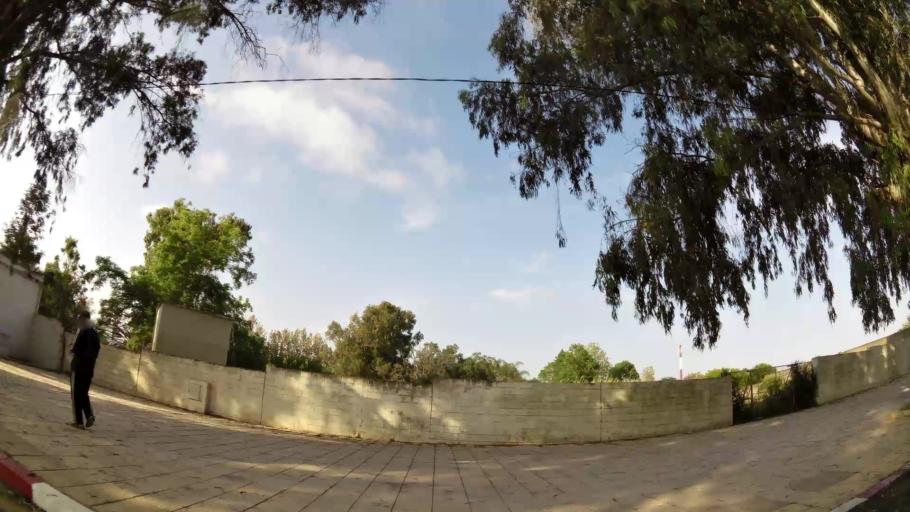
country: MA
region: Rabat-Sale-Zemmour-Zaer
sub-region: Rabat
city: Rabat
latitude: 33.9390
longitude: -6.8204
